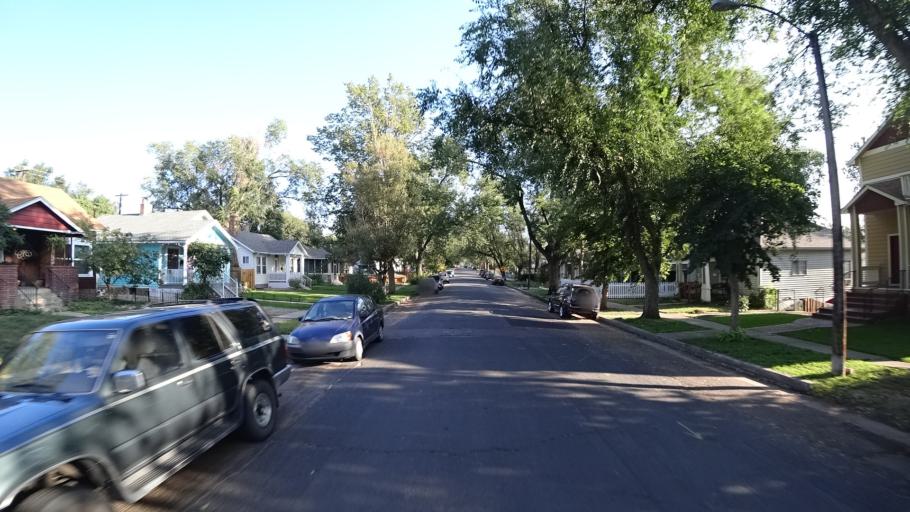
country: US
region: Colorado
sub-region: El Paso County
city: Colorado Springs
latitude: 38.8414
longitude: -104.8336
